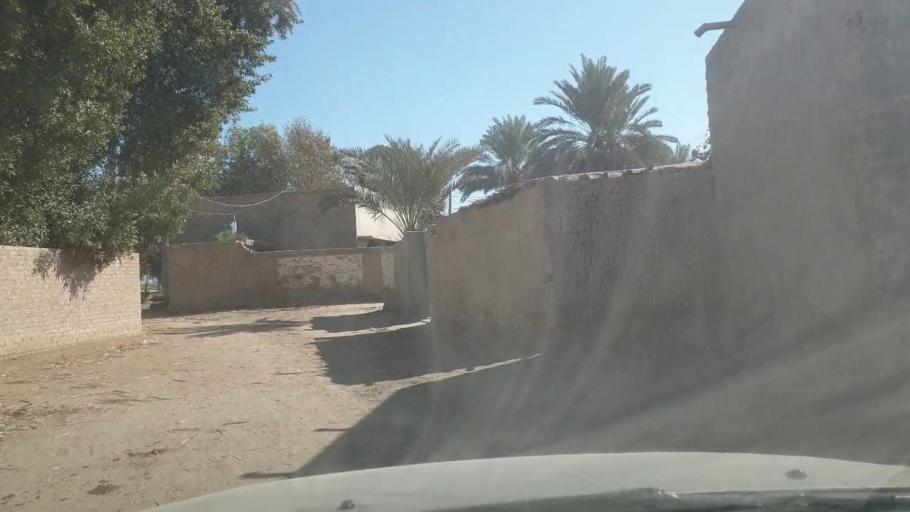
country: PK
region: Sindh
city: Ghotki
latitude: 28.0876
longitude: 69.3423
